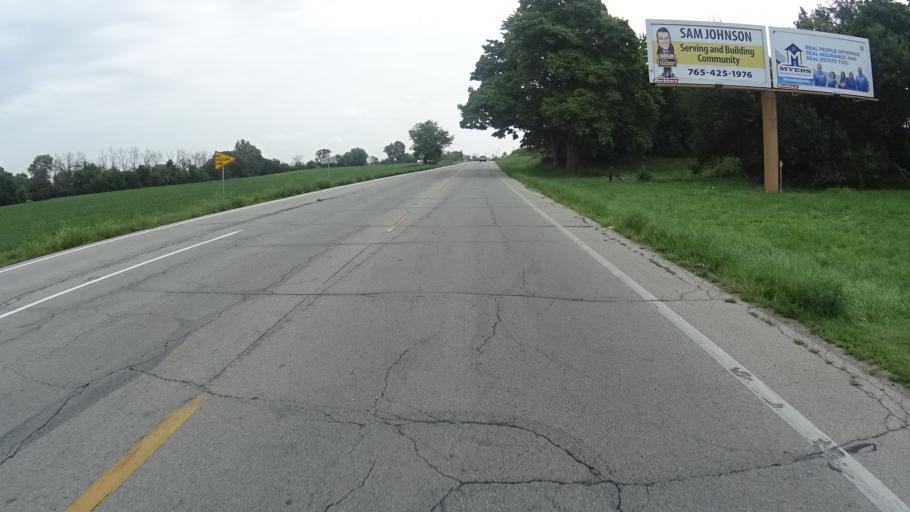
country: US
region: Indiana
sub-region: Madison County
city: Lapel
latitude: 40.0771
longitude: -85.8481
